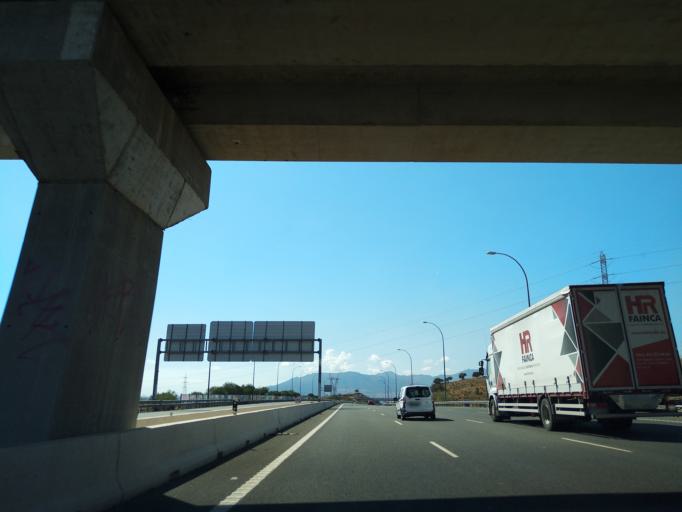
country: ES
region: Andalusia
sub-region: Provincia de Malaga
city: Malaga
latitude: 36.7429
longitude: -4.5025
